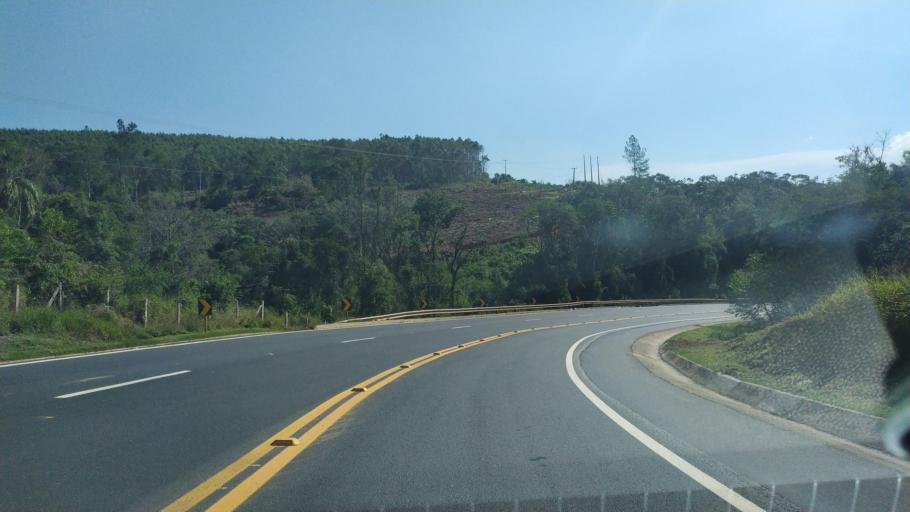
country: BR
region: Parana
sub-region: Telemaco Borba
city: Telemaco Borba
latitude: -24.2759
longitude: -50.7157
